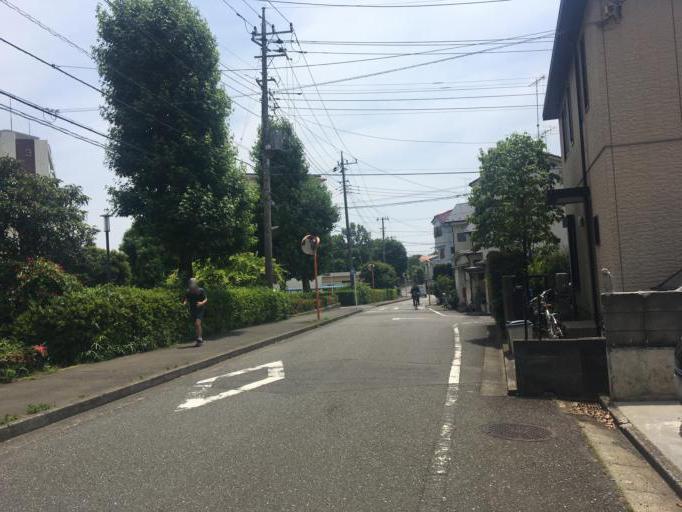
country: JP
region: Tokyo
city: Tanashicho
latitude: 35.7422
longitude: 139.5366
